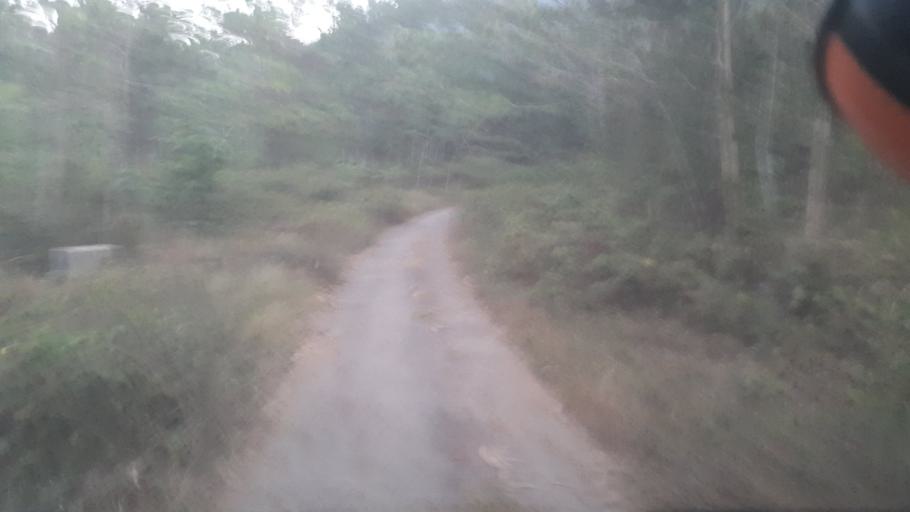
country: ID
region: West Java
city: Citarik
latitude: -6.9692
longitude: 106.6023
